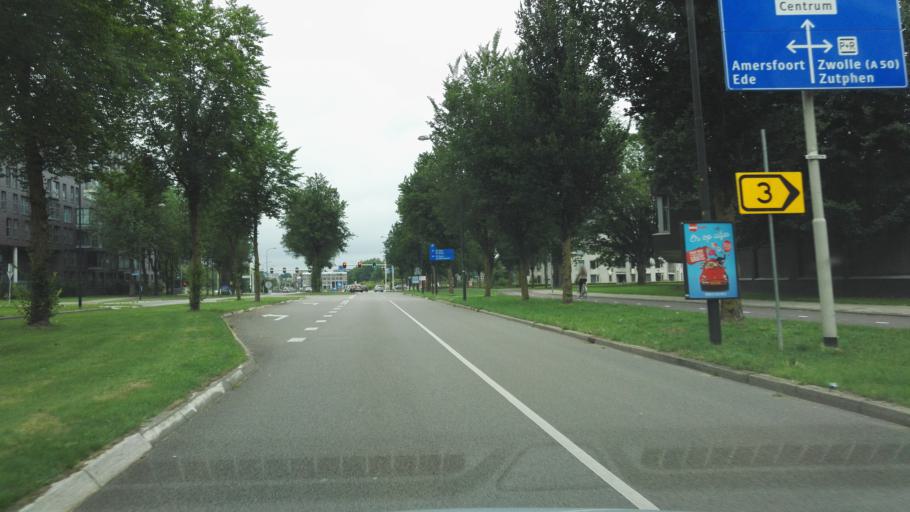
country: NL
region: Gelderland
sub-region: Gemeente Apeldoorn
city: Apeldoorn
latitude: 52.2037
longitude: 5.9588
